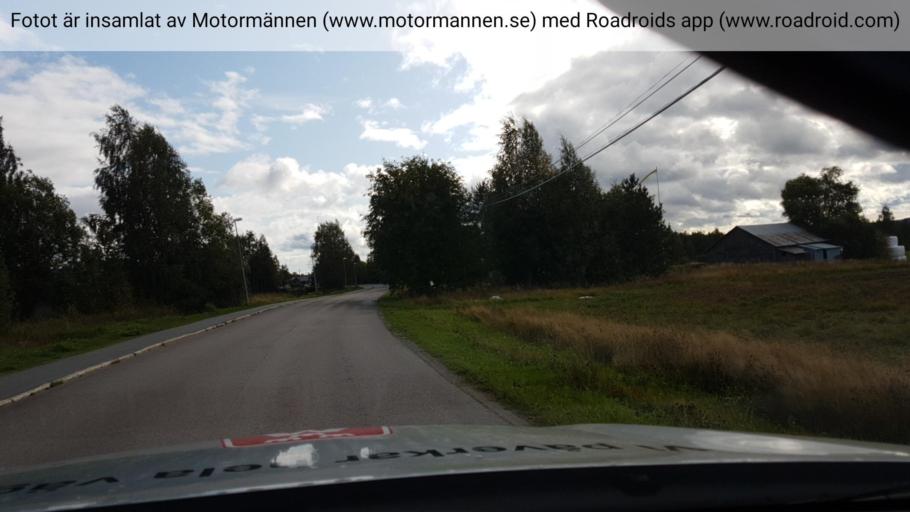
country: SE
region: Norrbotten
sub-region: Lulea Kommun
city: Sodra Sunderbyn
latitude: 65.6680
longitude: 21.9162
